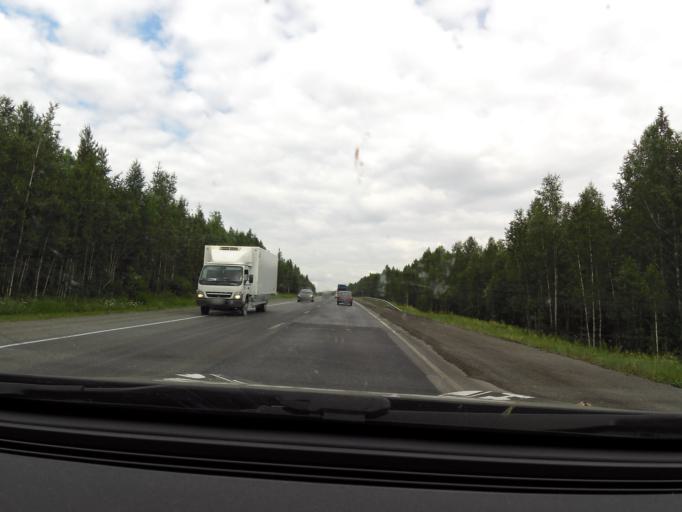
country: RU
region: Sverdlovsk
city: Druzhinino
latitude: 56.8397
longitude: 59.6609
